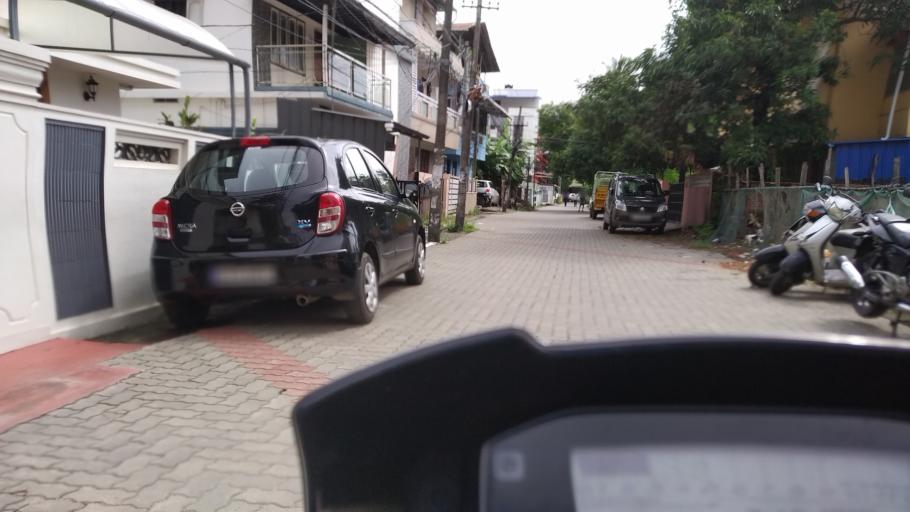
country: IN
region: Kerala
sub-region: Ernakulam
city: Cochin
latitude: 9.9792
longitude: 76.2951
